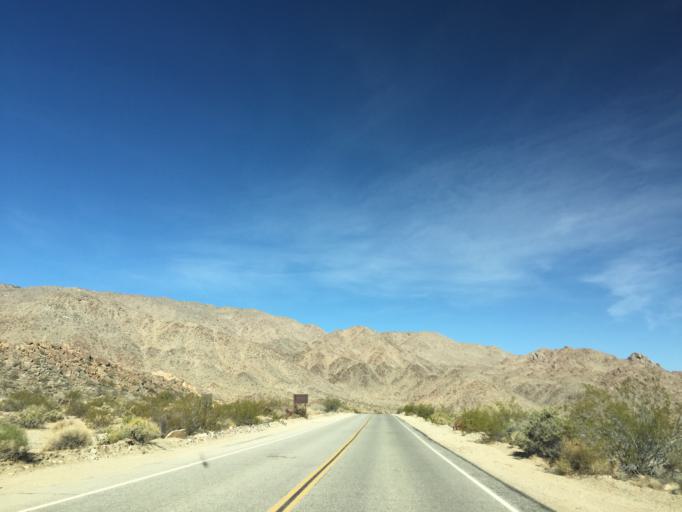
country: US
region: California
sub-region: San Bernardino County
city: Twentynine Palms
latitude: 34.0728
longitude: -116.0335
